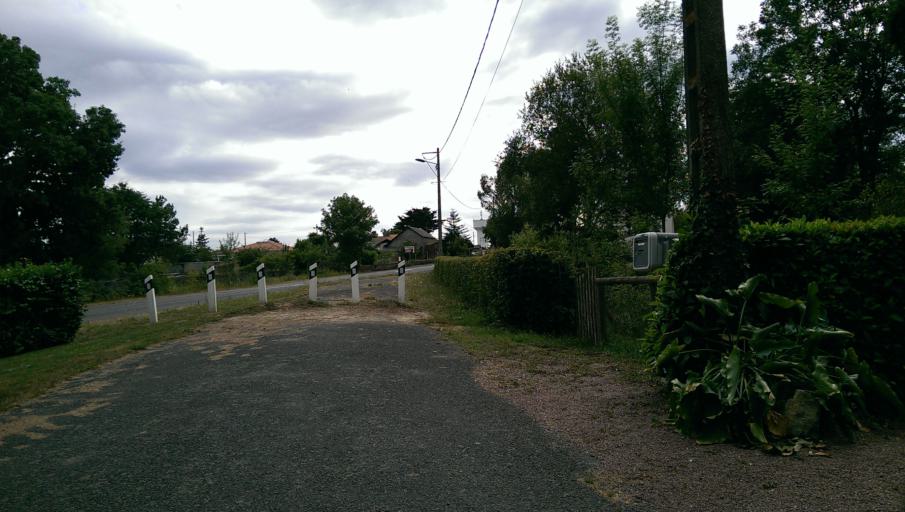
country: FR
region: Pays de la Loire
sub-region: Departement de la Loire-Atlantique
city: Vieillevigne
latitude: 46.9755
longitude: -1.4334
